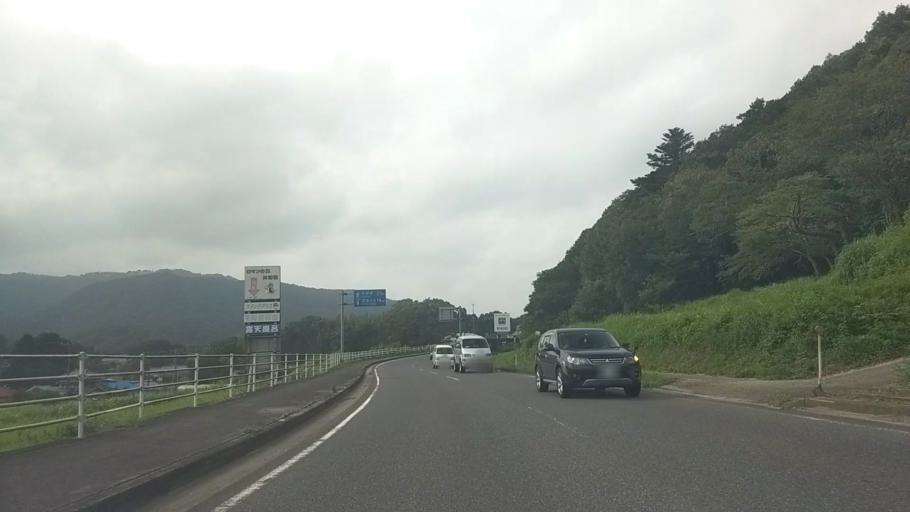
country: JP
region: Chiba
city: Kimitsu
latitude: 35.2488
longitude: 140.0024
